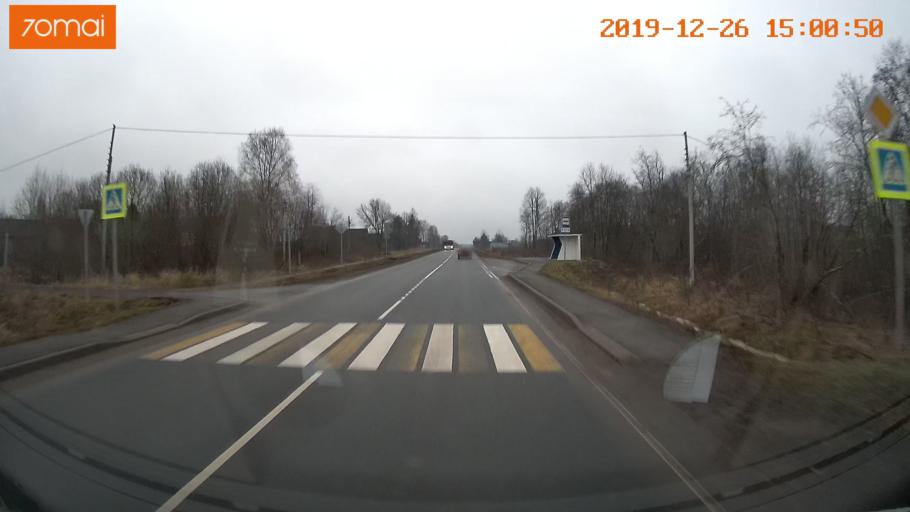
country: RU
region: Jaroslavl
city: Rybinsk
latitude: 58.2424
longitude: 38.8576
